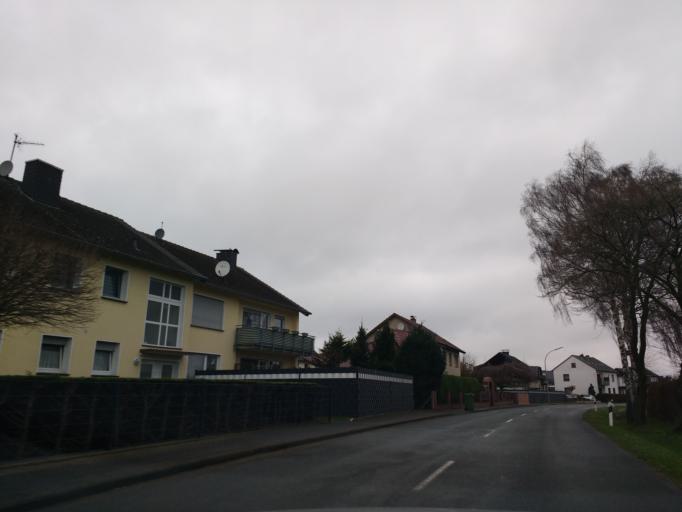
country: DE
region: North Rhine-Westphalia
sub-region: Regierungsbezirk Detmold
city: Salzkotten
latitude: 51.6768
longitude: 8.5631
